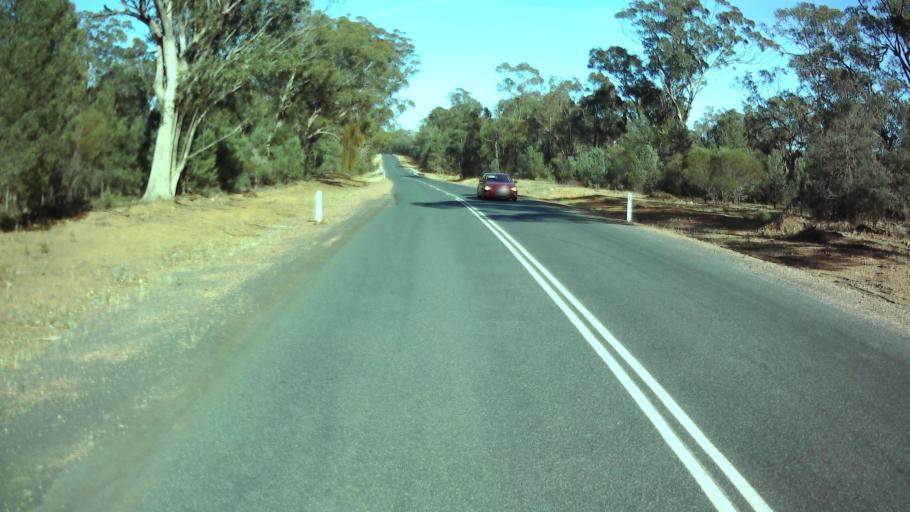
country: AU
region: New South Wales
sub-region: Weddin
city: Grenfell
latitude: -34.0299
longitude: 148.0685
